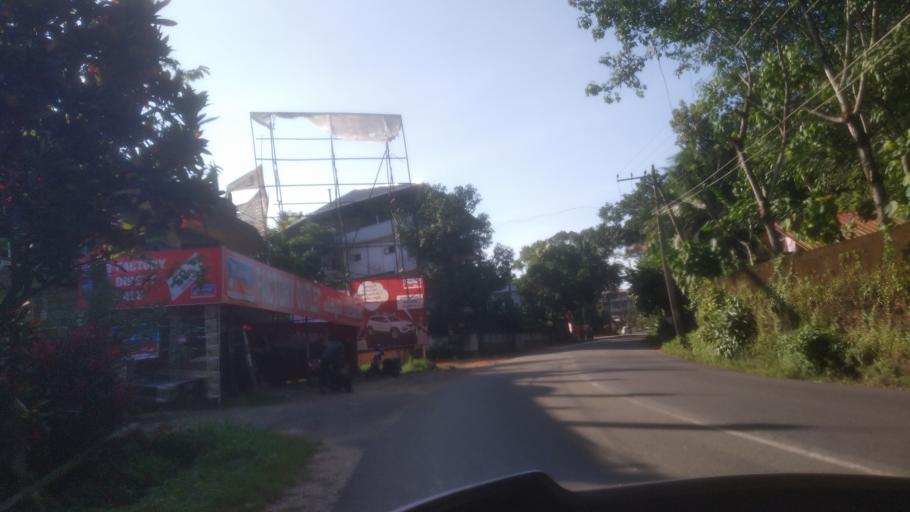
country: IN
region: Kerala
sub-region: Ernakulam
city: Ramamangalam
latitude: 9.9778
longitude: 76.4901
